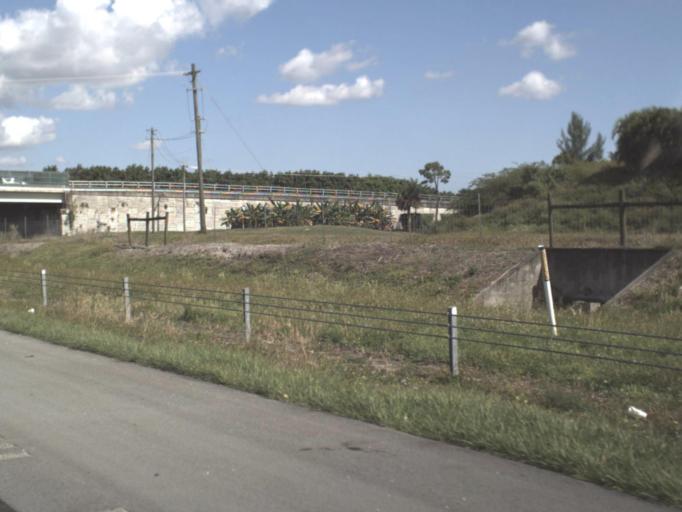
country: US
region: Florida
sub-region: Palm Beach County
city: Boca Del Mar
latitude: 26.3929
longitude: -80.1710
